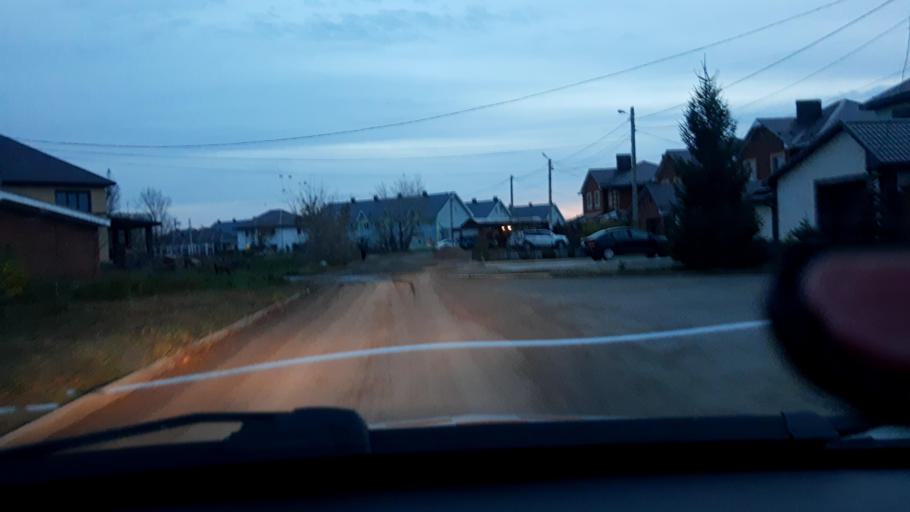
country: RU
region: Bashkortostan
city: Ufa
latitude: 54.6876
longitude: 55.9783
